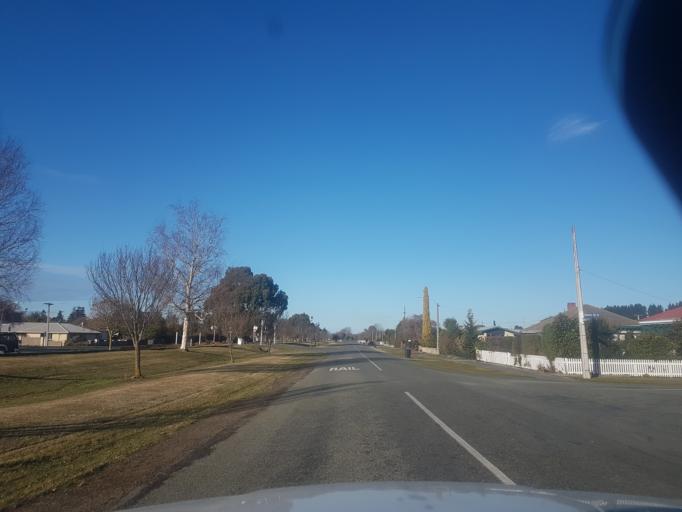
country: NZ
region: Canterbury
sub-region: Timaru District
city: Pleasant Point
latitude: -44.2625
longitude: 171.1351
